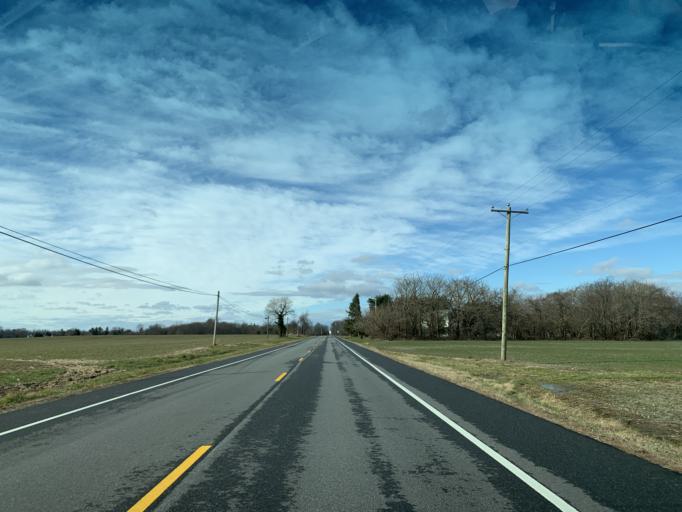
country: US
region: Maryland
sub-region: Kent County
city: Chestertown
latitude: 39.3259
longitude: -76.0334
